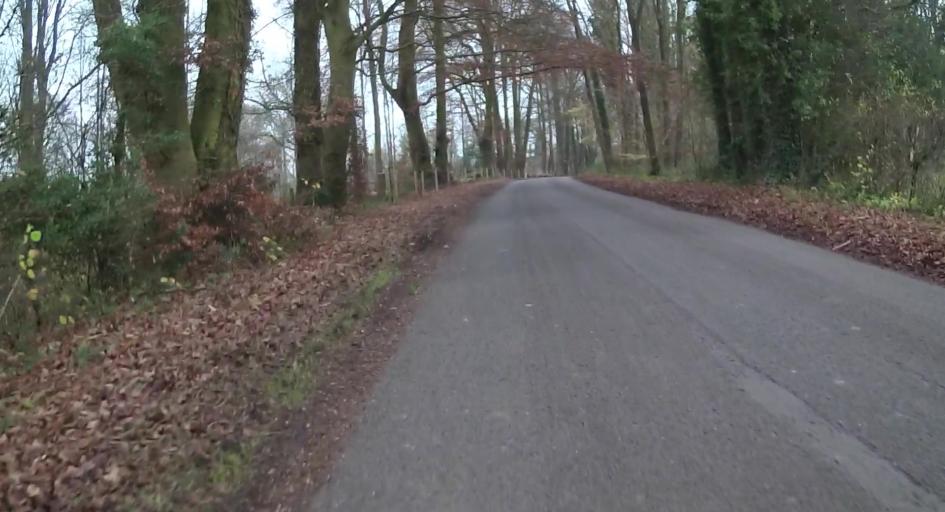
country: GB
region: England
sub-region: Hampshire
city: Kings Worthy
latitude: 51.1181
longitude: -1.2108
